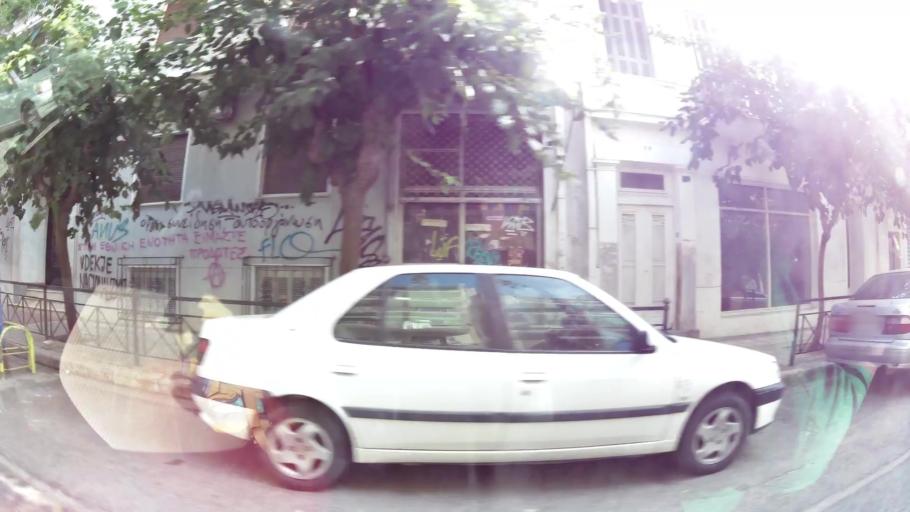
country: GR
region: Attica
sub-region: Nomarchia Athinas
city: Kipseli
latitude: 37.9969
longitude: 23.7300
